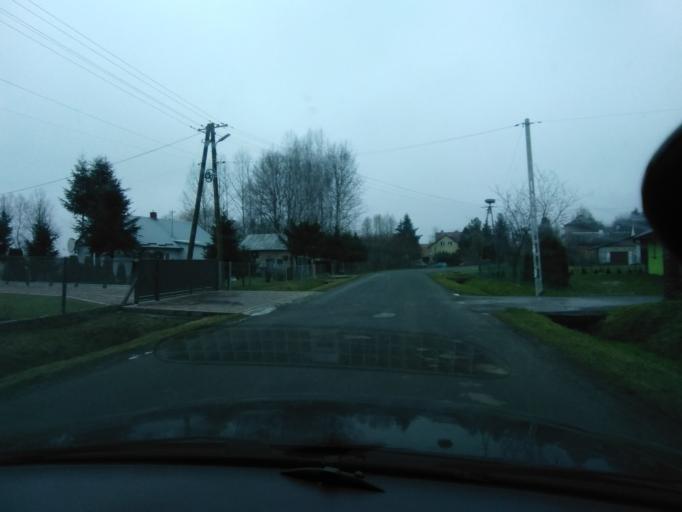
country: PL
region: Subcarpathian Voivodeship
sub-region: Powiat przeworski
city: Zarzecze
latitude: 49.9563
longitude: 22.5663
